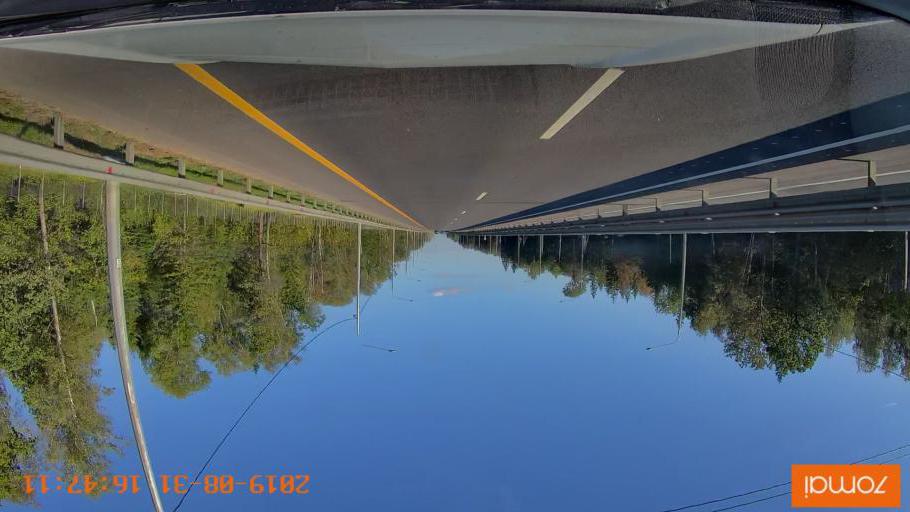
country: RU
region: Kaluga
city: Pyatovskiy
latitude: 54.6496
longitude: 36.1369
